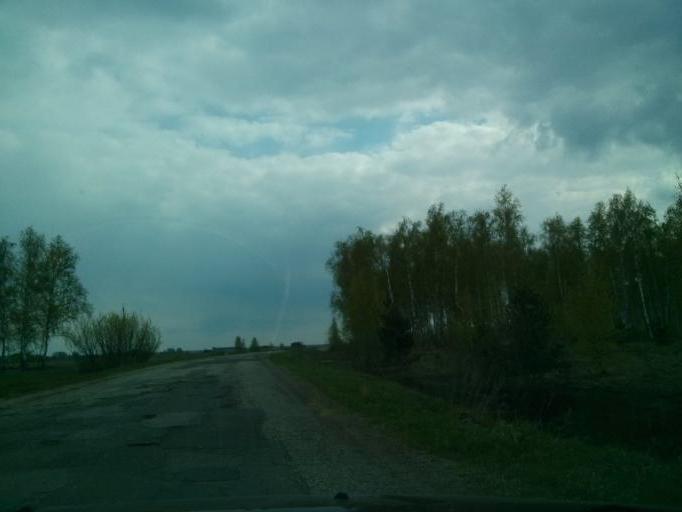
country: RU
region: Vladimir
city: Melenki
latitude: 55.3260
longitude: 41.7768
